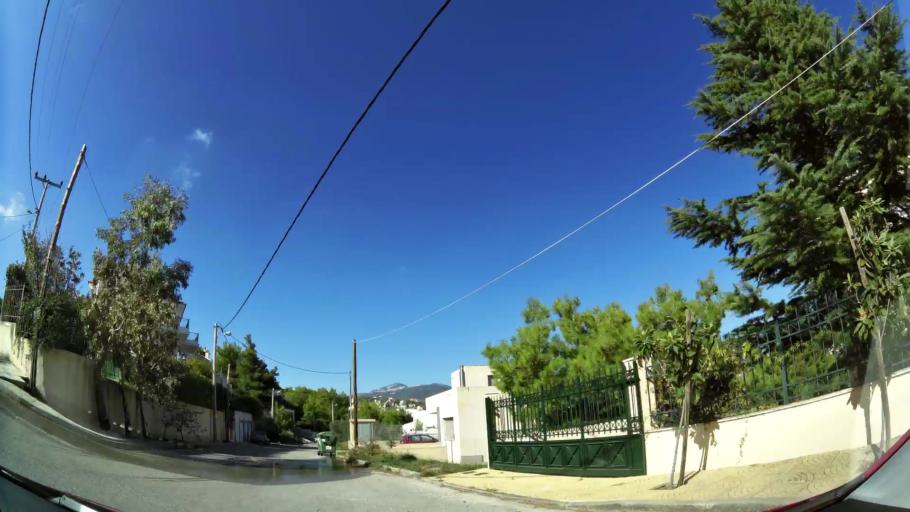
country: GR
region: Attica
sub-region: Nomarchia Anatolikis Attikis
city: Dhrafi
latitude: 38.0065
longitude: 23.9185
